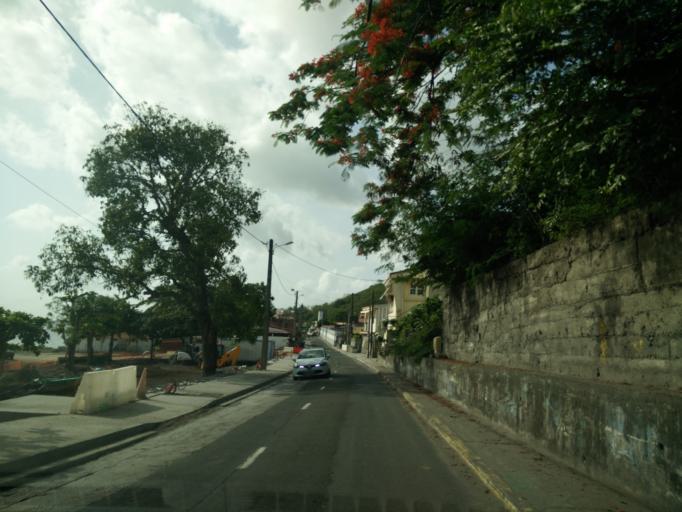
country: MQ
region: Martinique
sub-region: Martinique
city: Saint-Pierre
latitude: 14.7935
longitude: -61.2200
